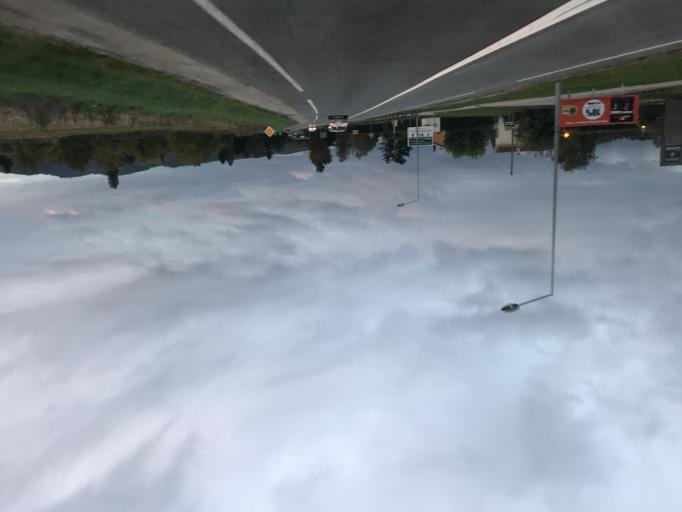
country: FR
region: Rhone-Alpes
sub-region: Departement de l'Ain
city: Reyrieux
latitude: 45.9274
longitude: 4.8116
